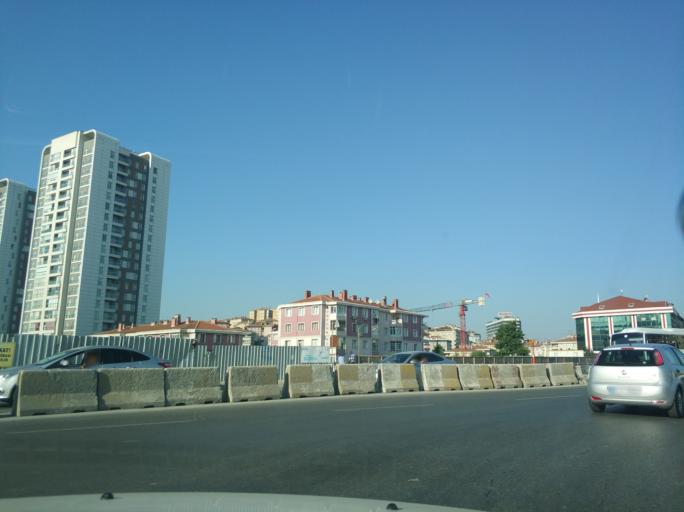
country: TR
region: Istanbul
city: Sultangazi
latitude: 41.0851
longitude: 28.9079
